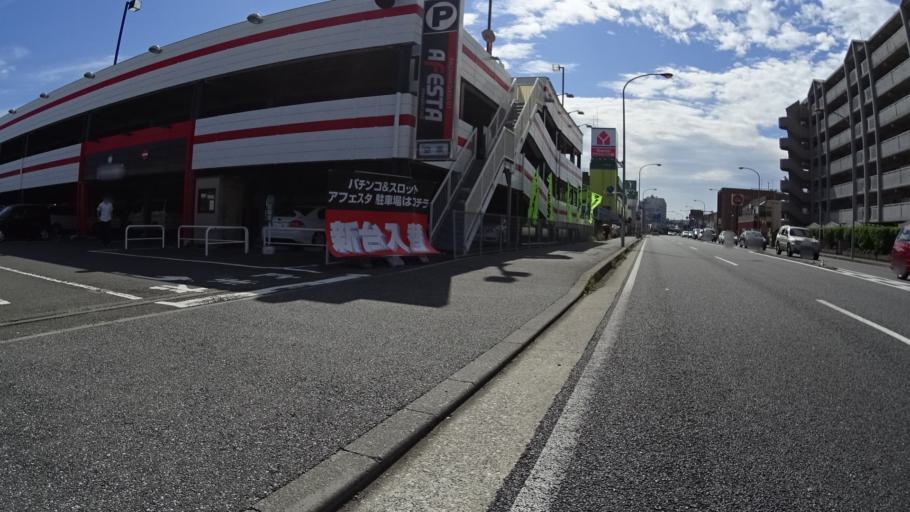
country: JP
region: Kanagawa
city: Yokosuka
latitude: 35.2650
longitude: 139.6905
